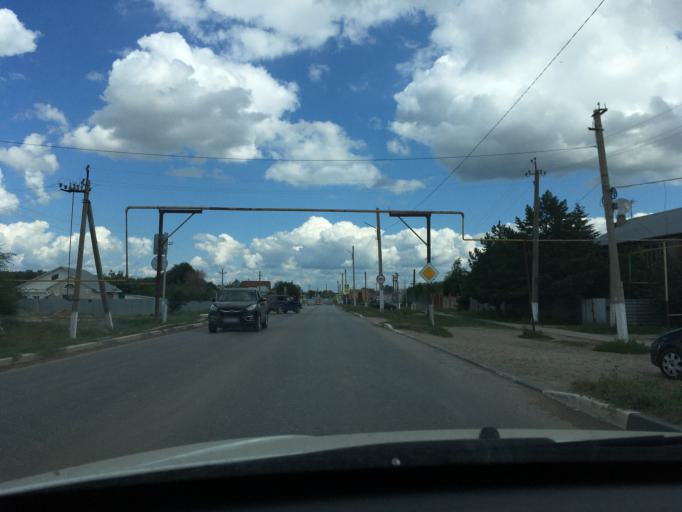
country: RU
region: Samara
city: Bezenchuk
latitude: 52.9898
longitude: 49.4359
